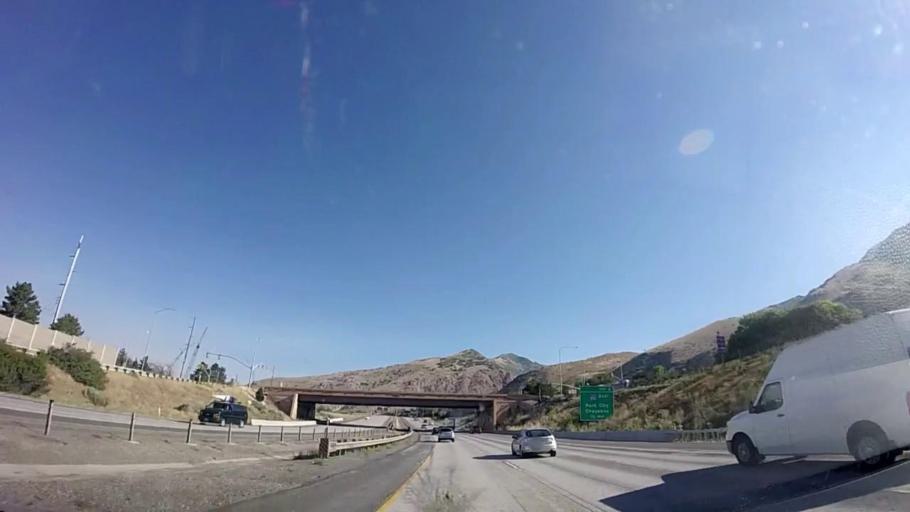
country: US
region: Utah
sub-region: Salt Lake County
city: Mount Olympus
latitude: 40.6986
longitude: -111.7953
